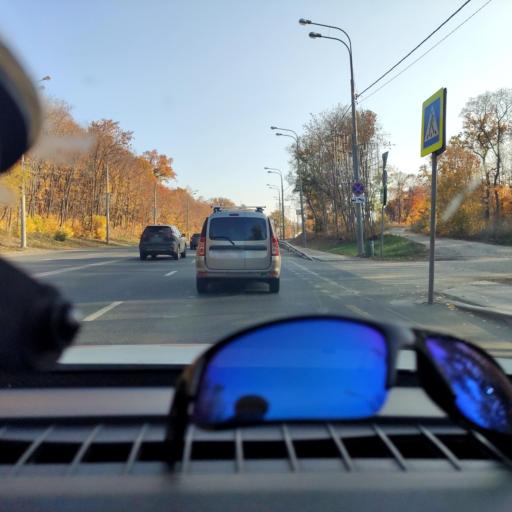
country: RU
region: Samara
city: Samara
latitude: 53.2827
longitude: 50.2282
